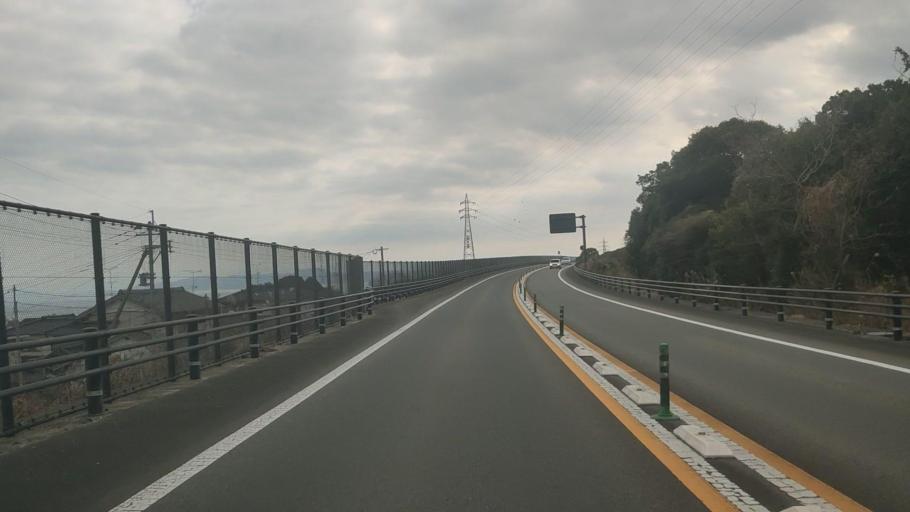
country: JP
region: Nagasaki
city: Shimabara
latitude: 32.7835
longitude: 130.3528
